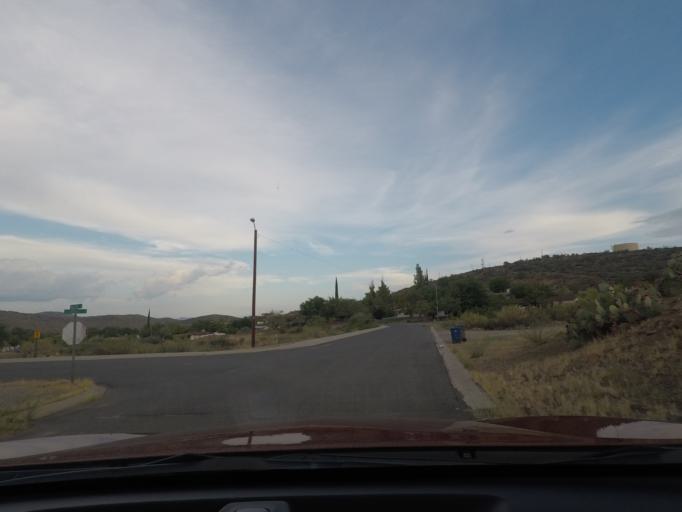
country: US
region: Arizona
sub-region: Yavapai County
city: Bagdad
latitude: 34.5727
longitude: -113.1837
